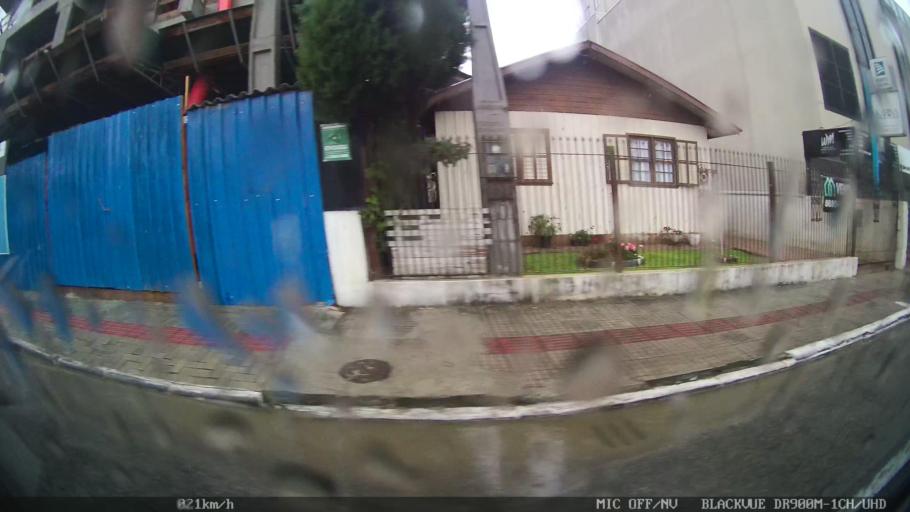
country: BR
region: Santa Catarina
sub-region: Itajai
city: Itajai
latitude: -26.9066
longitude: -48.6691
